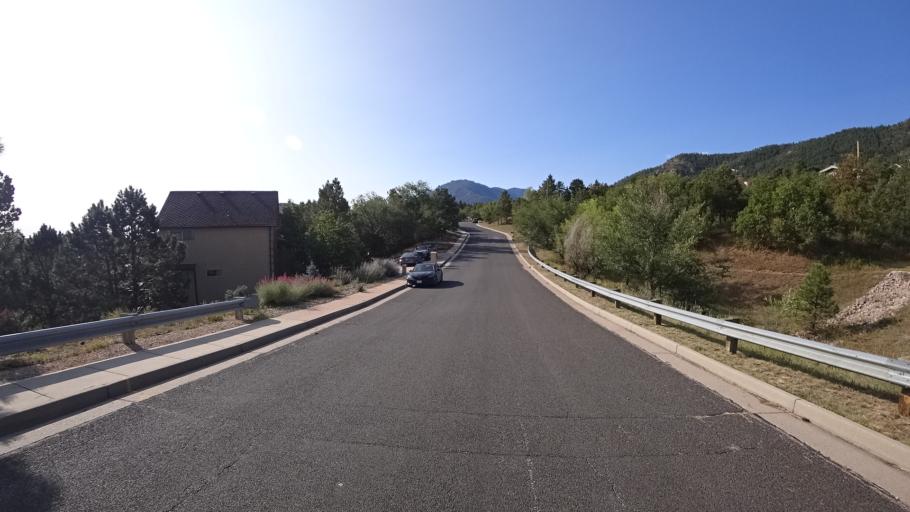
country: US
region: Colorado
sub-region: El Paso County
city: Colorado Springs
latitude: 38.8125
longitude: -104.8708
